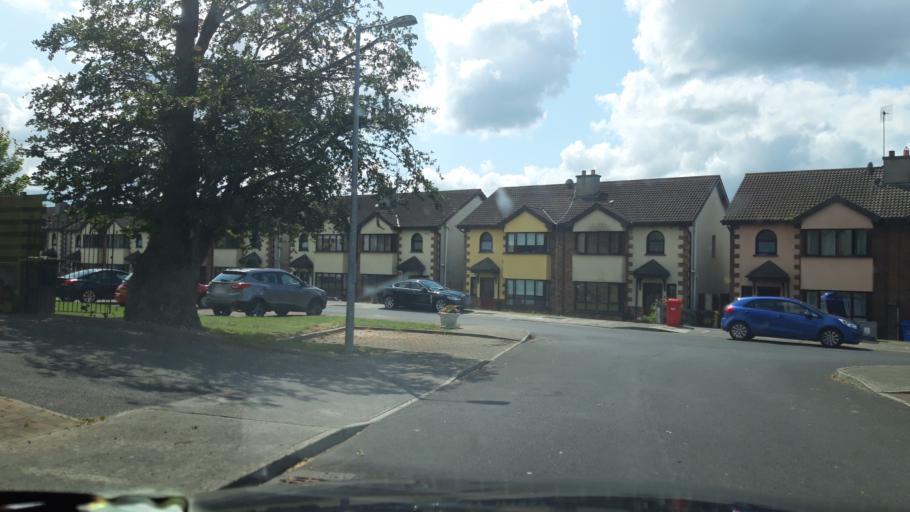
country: IE
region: Munster
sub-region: Waterford
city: Waterford
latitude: 52.2674
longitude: -7.0923
